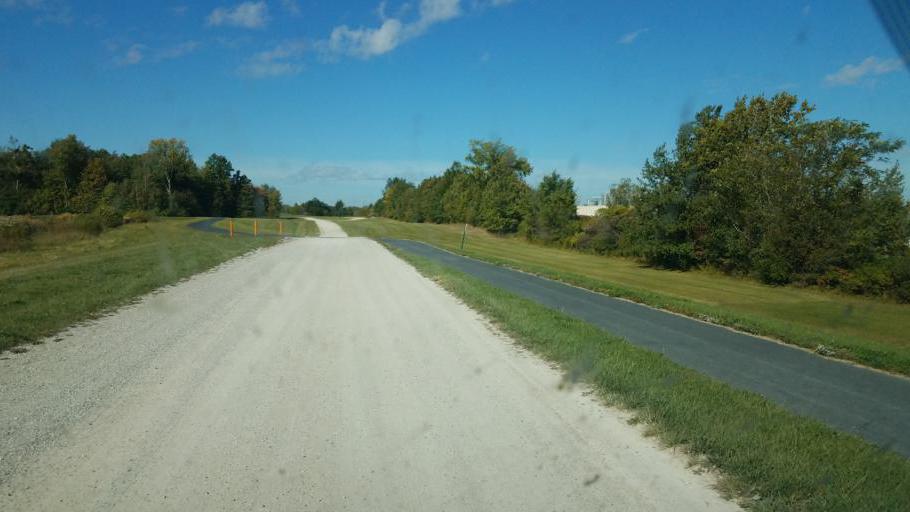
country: US
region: Ohio
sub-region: Wyandot County
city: Upper Sandusky
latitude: 40.8236
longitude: -83.2515
